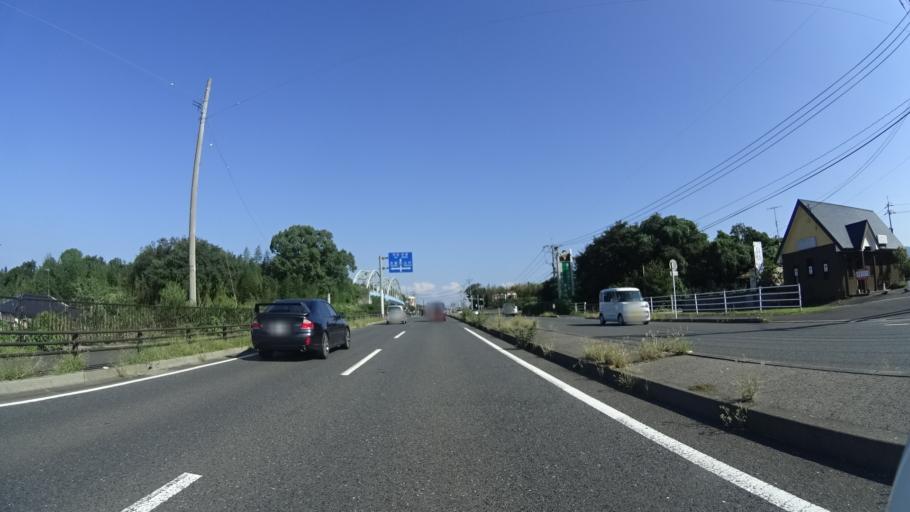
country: JP
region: Fukuoka
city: Yoshitomi
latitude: 33.5912
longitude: 131.1503
